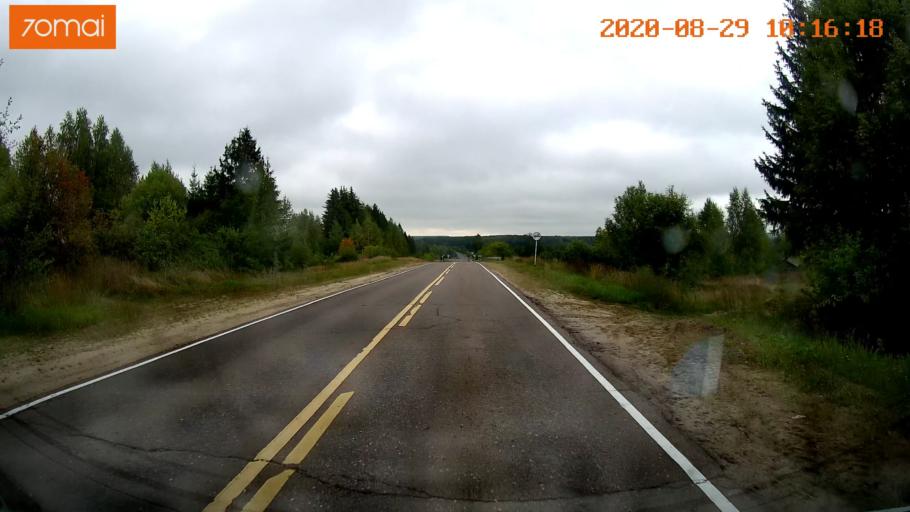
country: RU
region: Ivanovo
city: Yur'yevets
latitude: 57.3388
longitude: 42.7900
